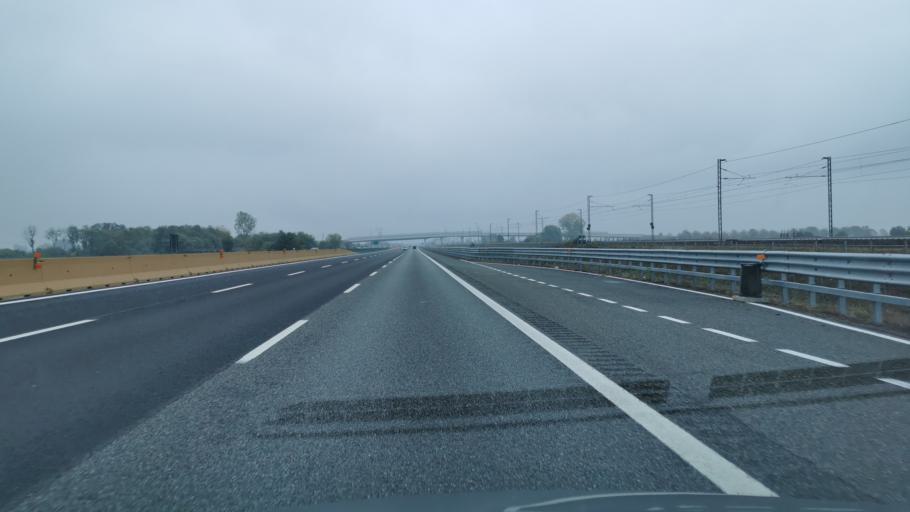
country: IT
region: Piedmont
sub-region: Provincia di Vercelli
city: Saluggia
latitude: 45.2719
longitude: 8.0192
